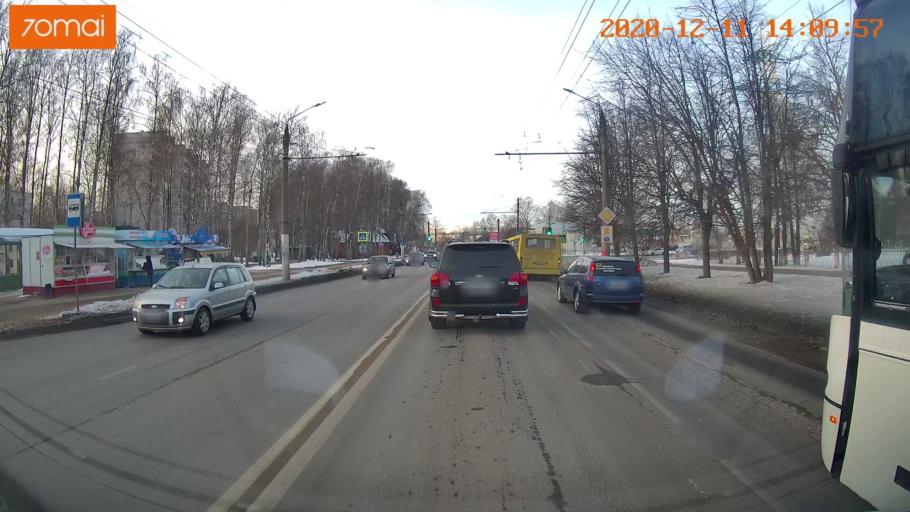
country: RU
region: Kostroma
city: Oktyabr'skiy
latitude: 57.7393
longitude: 40.9869
